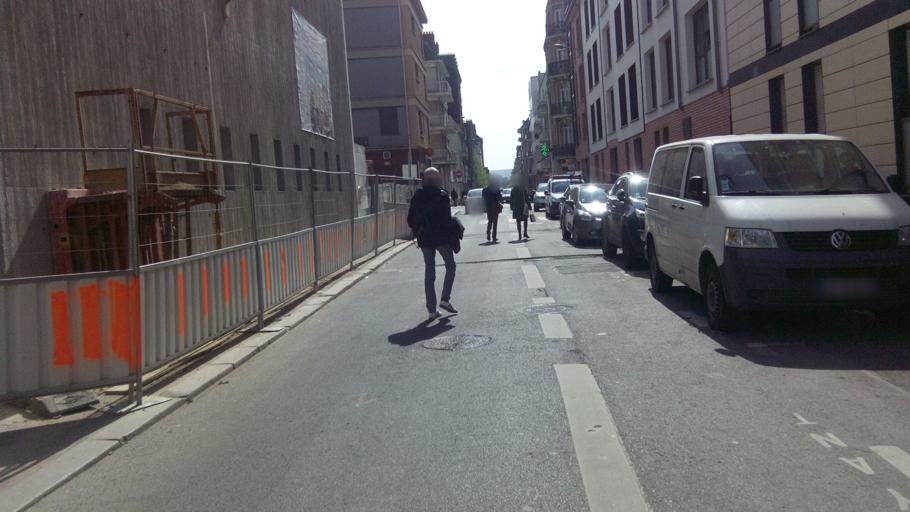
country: FR
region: Haute-Normandie
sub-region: Departement de la Seine-Maritime
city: Rouen
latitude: 49.4330
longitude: 1.0887
